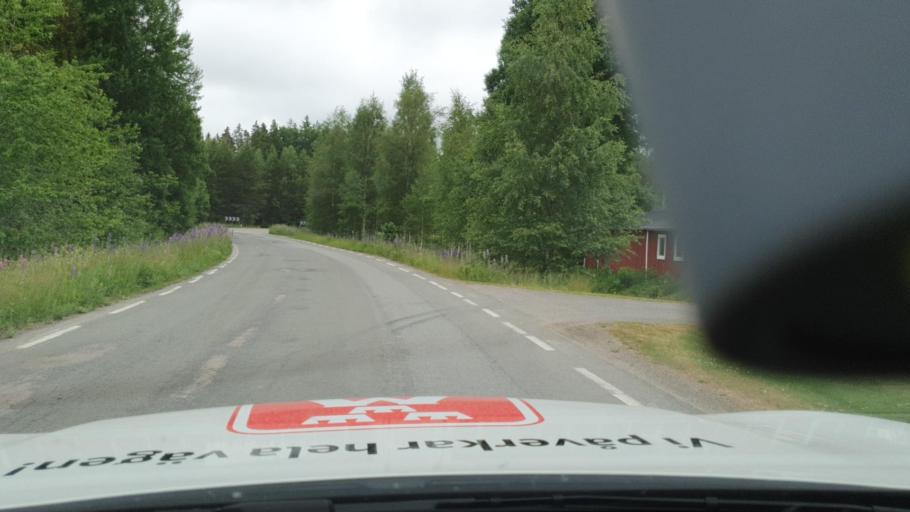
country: SE
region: Vaestra Goetaland
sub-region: Tibro Kommun
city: Tibro
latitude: 58.3748
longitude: 14.2023
